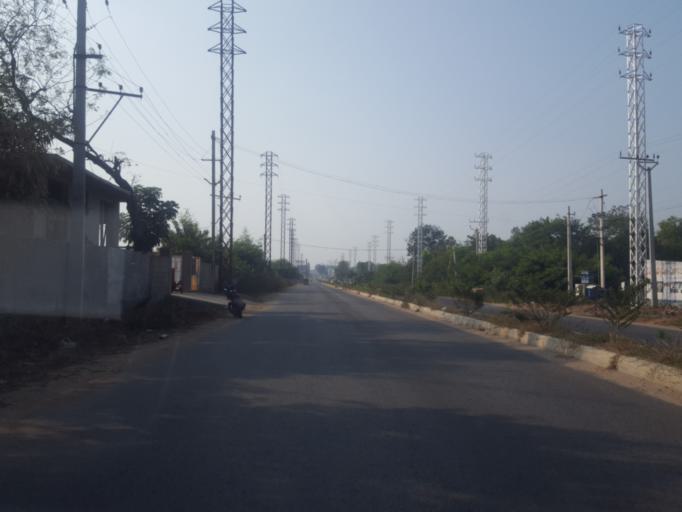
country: IN
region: Telangana
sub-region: Medak
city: Serilingampalle
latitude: 17.4014
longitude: 78.2932
